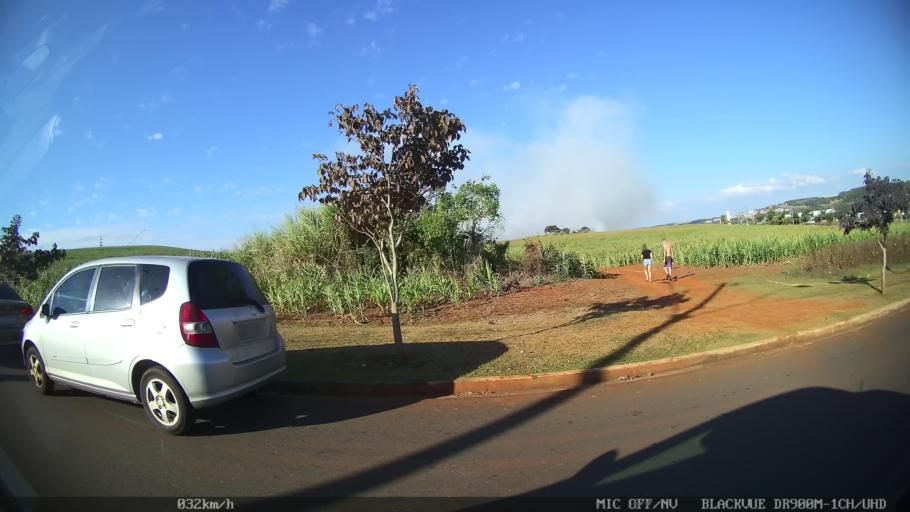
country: BR
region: Sao Paulo
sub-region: Piracicaba
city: Piracicaba
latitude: -22.6943
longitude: -47.6154
